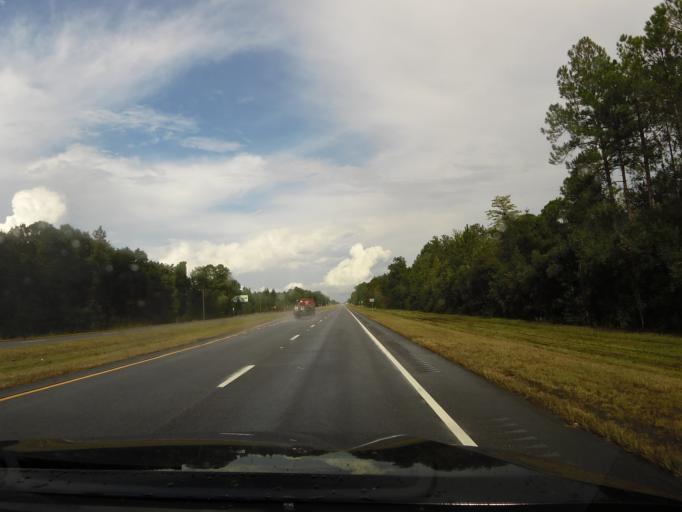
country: US
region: Georgia
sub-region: Liberty County
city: Walthourville
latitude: 31.7481
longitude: -81.6804
